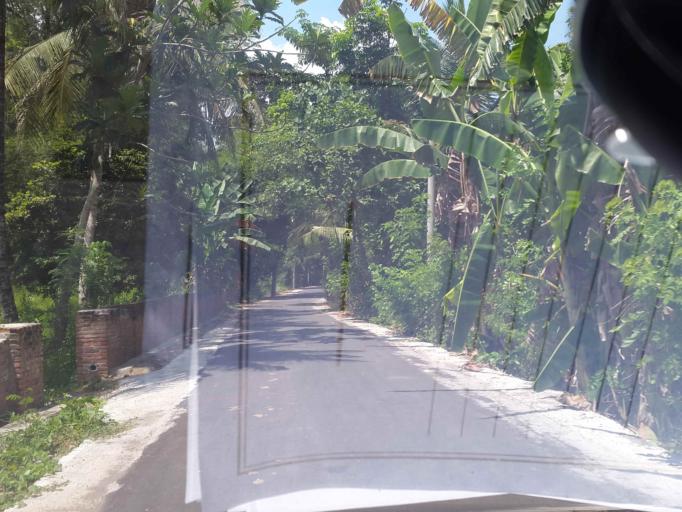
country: ID
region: West Nusa Tenggara
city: Jelateng Timur
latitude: -8.7125
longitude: 116.0742
